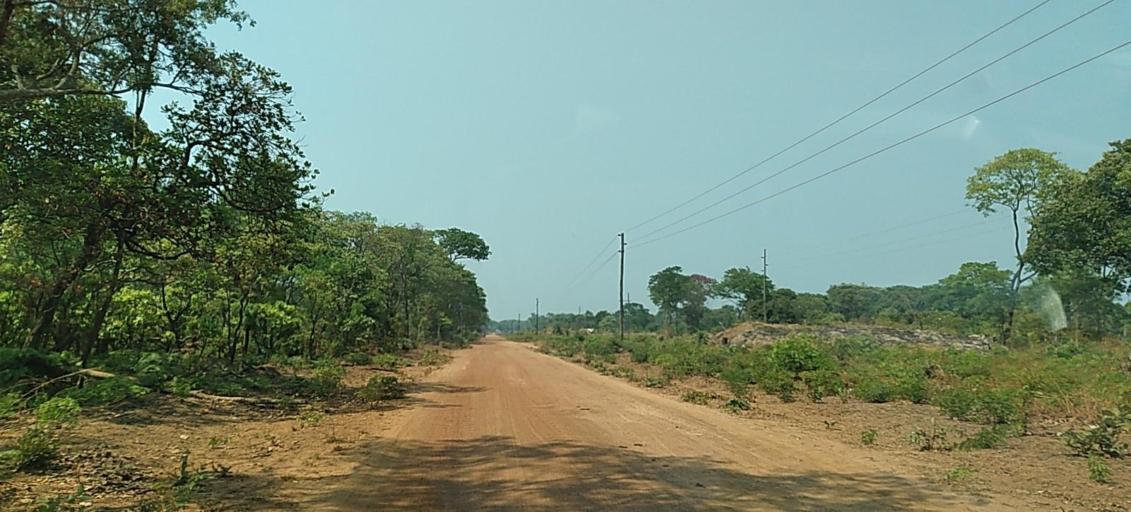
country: ZM
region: Copperbelt
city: Kalulushi
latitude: -13.0982
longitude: 27.4051
